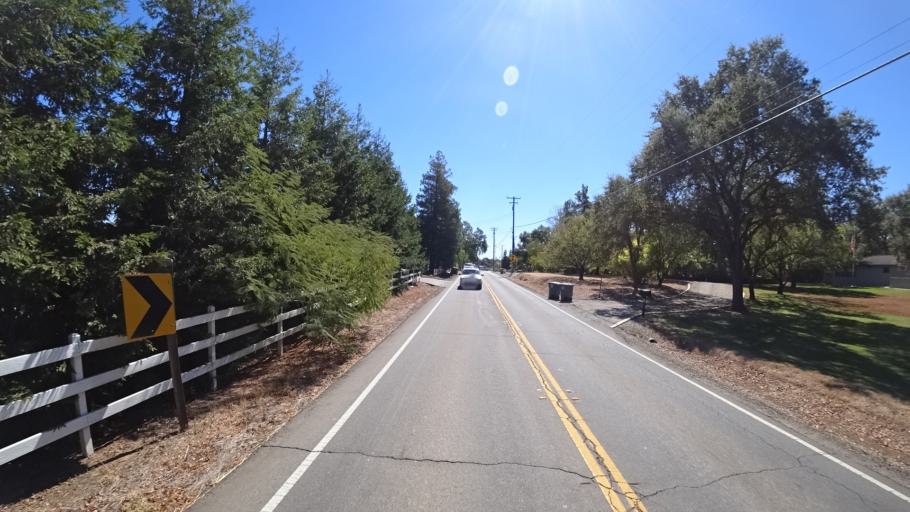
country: US
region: California
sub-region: Sacramento County
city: Wilton
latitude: 38.4376
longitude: -121.2969
